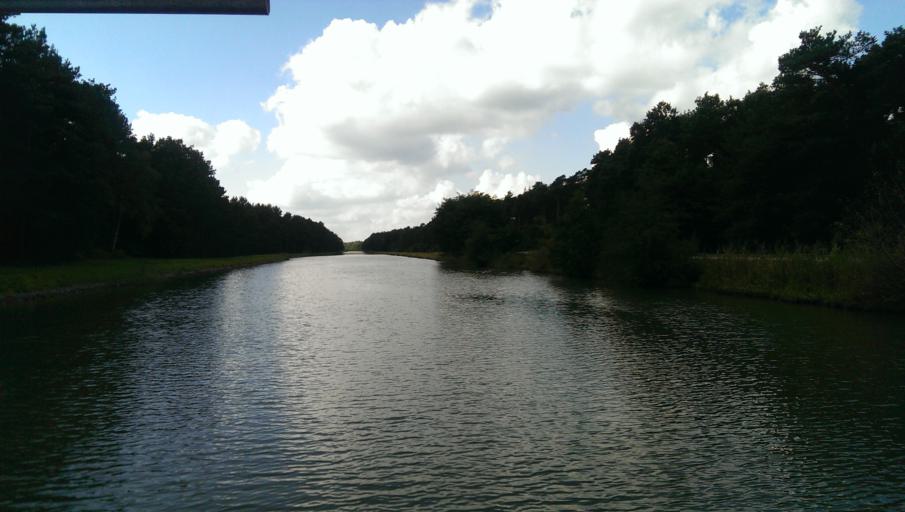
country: DE
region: Brandenburg
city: Melchow
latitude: 52.8591
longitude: 13.7219
